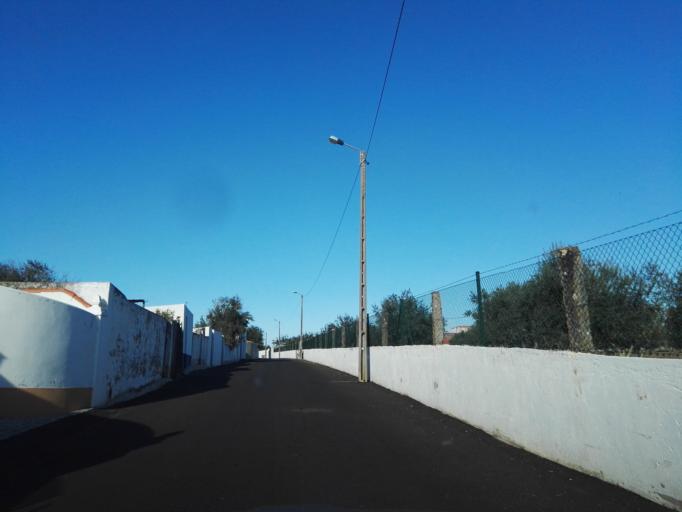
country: PT
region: Evora
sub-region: Arraiolos
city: Arraiolos
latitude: 38.7053
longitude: -7.8971
